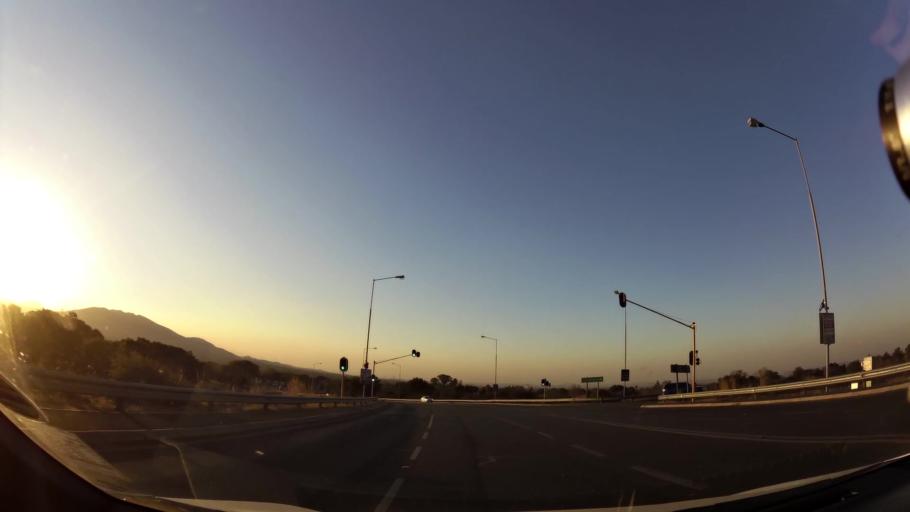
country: ZA
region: North-West
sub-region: Bojanala Platinum District Municipality
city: Rustenburg
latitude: -25.6891
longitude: 27.2264
